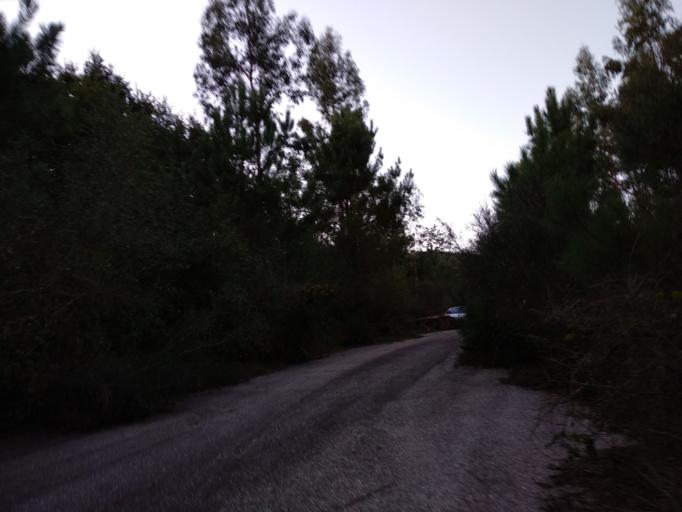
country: ES
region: Galicia
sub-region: Provincia de Pontevedra
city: Moana
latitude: 42.3012
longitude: -8.6955
